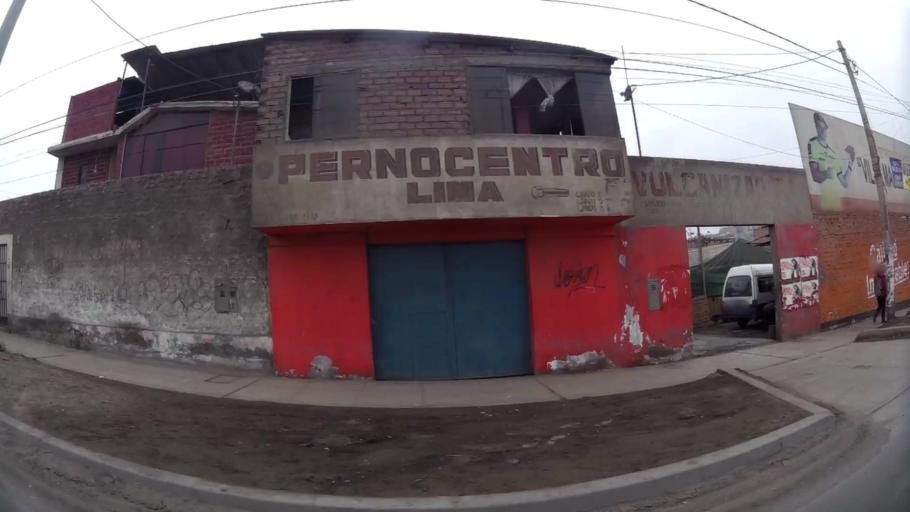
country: PE
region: Lima
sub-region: Lima
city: Surco
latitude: -12.2273
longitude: -76.9091
